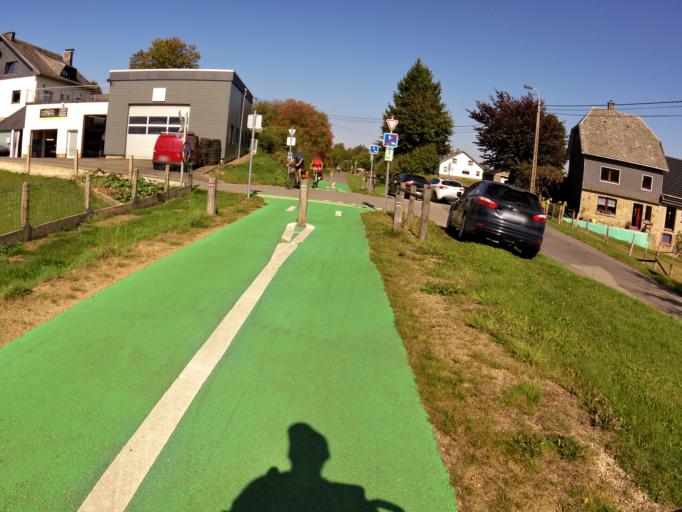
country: BE
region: Wallonia
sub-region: Province de Liege
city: Butgenbach
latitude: 50.4324
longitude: 6.1729
